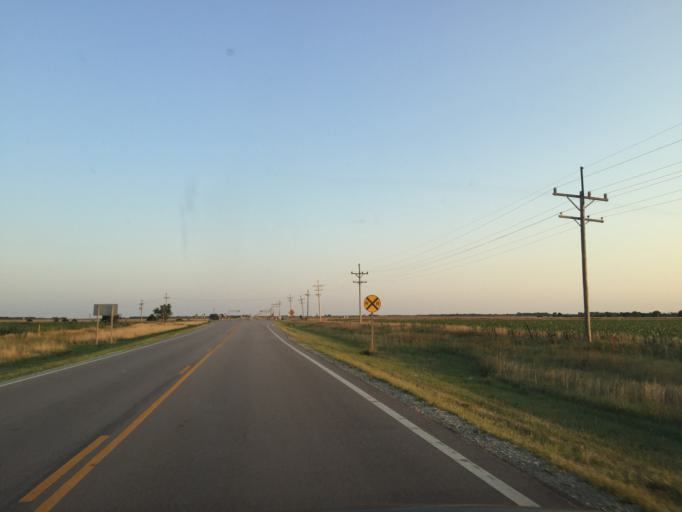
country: US
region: Kansas
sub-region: Rice County
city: Lyons
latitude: 38.5191
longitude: -98.2015
